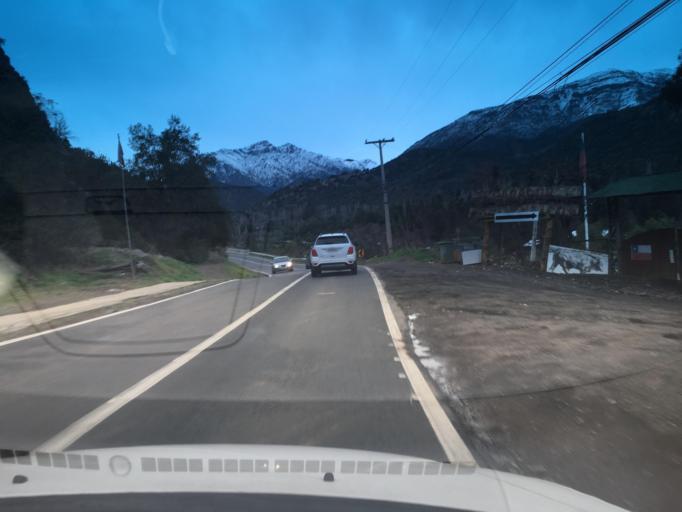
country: CL
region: Santiago Metropolitan
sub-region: Provincia de Cordillera
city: Puente Alto
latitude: -33.6671
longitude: -70.3494
